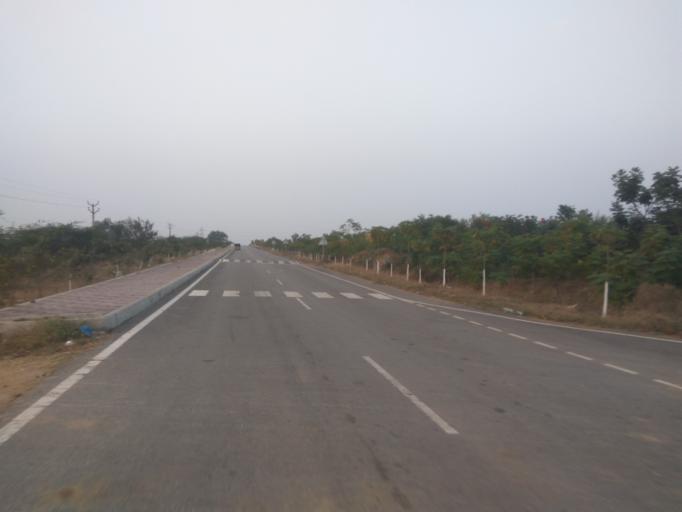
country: IN
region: Telangana
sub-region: Rangareddi
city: Secunderabad
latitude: 17.5423
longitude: 78.6308
